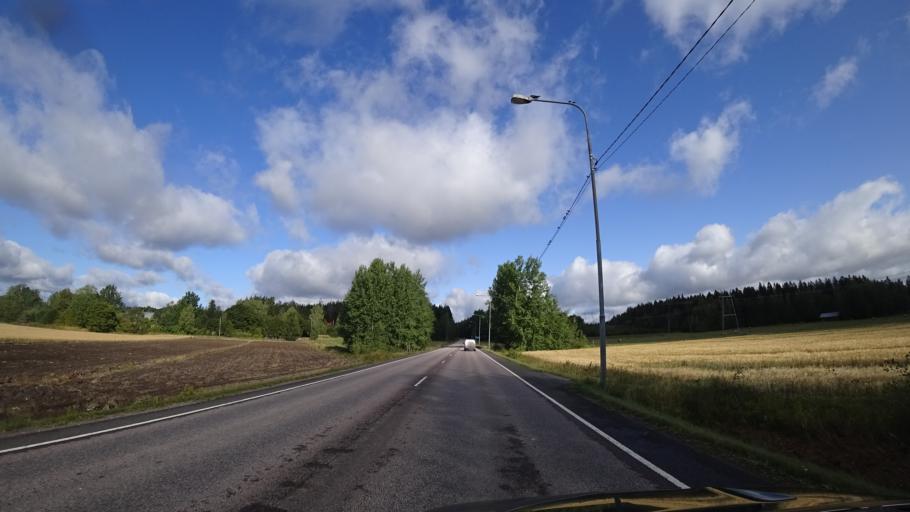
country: FI
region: Uusimaa
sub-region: Helsinki
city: Hyvinge
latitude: 60.5285
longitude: 24.9229
